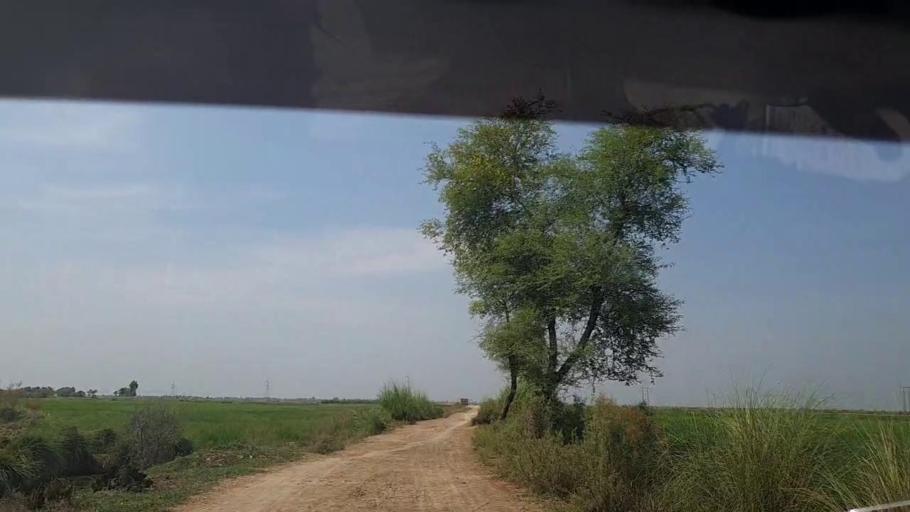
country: PK
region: Sindh
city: Thul
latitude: 28.2192
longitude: 68.6764
